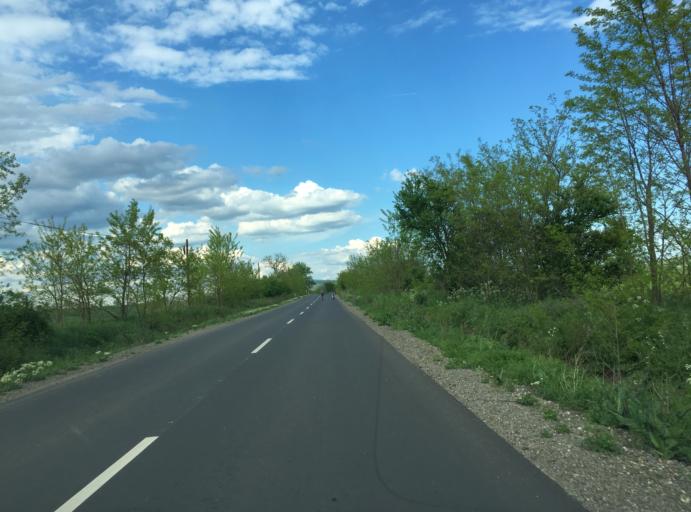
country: HU
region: Heves
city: Lorinci
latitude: 47.7249
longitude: 19.6564
